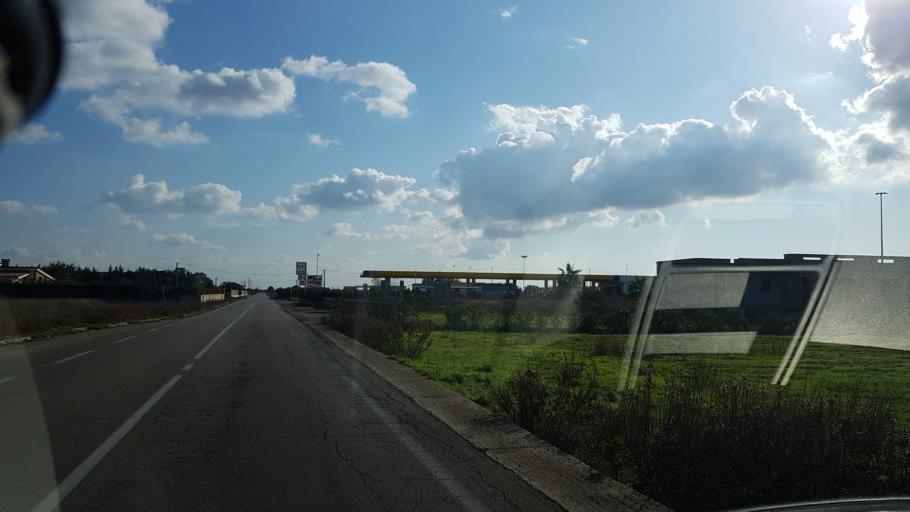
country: IT
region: Apulia
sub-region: Provincia di Lecce
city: Veglie
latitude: 40.3229
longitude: 17.9776
